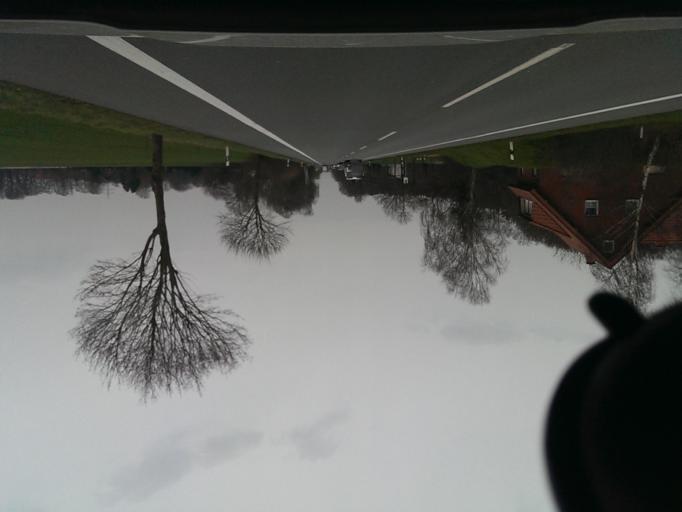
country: DE
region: North Rhine-Westphalia
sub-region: Regierungsbezirk Detmold
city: Hovelhof
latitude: 51.7619
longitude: 8.6250
